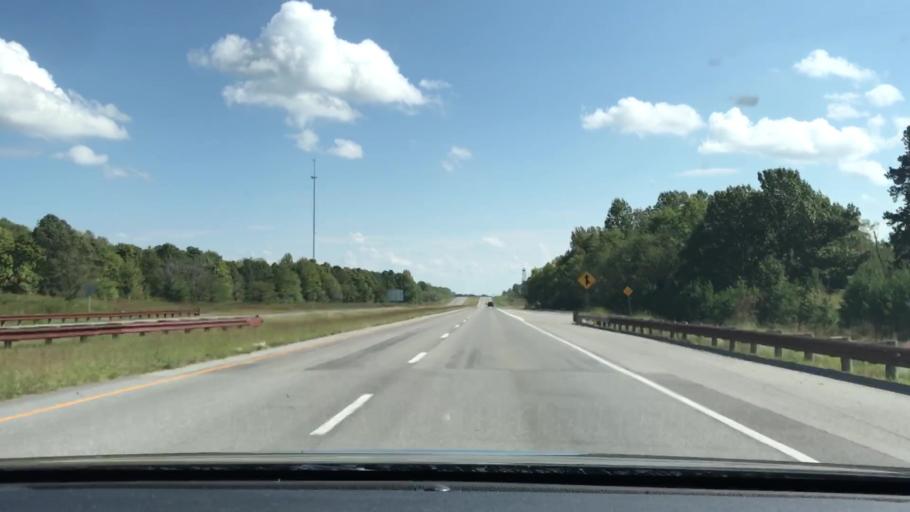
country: US
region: Kentucky
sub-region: Trigg County
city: Cadiz
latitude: 36.7794
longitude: -88.0657
